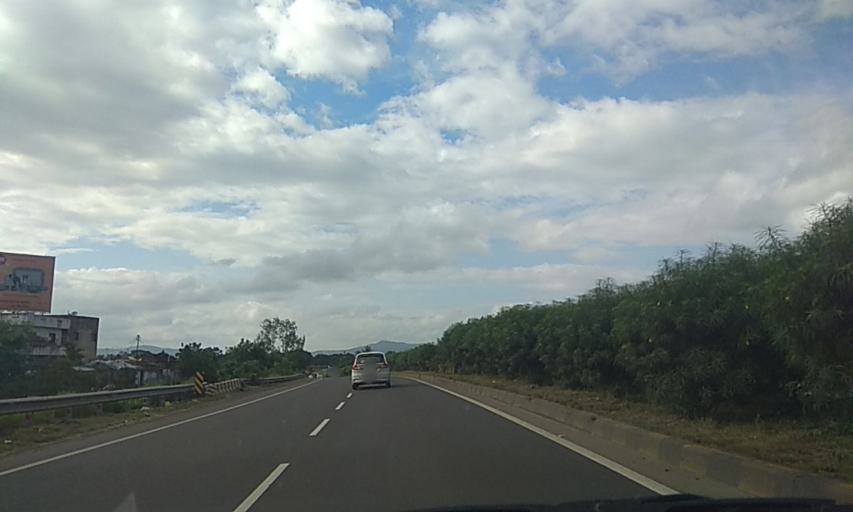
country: IN
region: Maharashtra
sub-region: Satara Division
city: Karad
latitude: 17.1265
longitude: 74.1913
